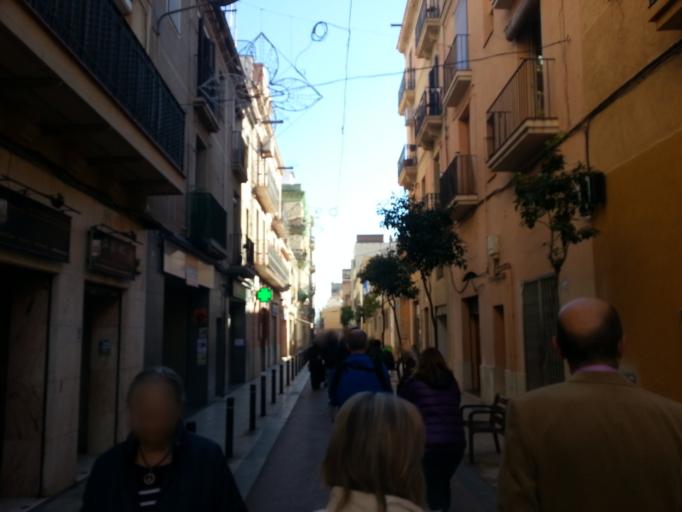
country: ES
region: Catalonia
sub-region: Provincia de Barcelona
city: Sant Marti
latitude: 41.4002
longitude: 2.2049
